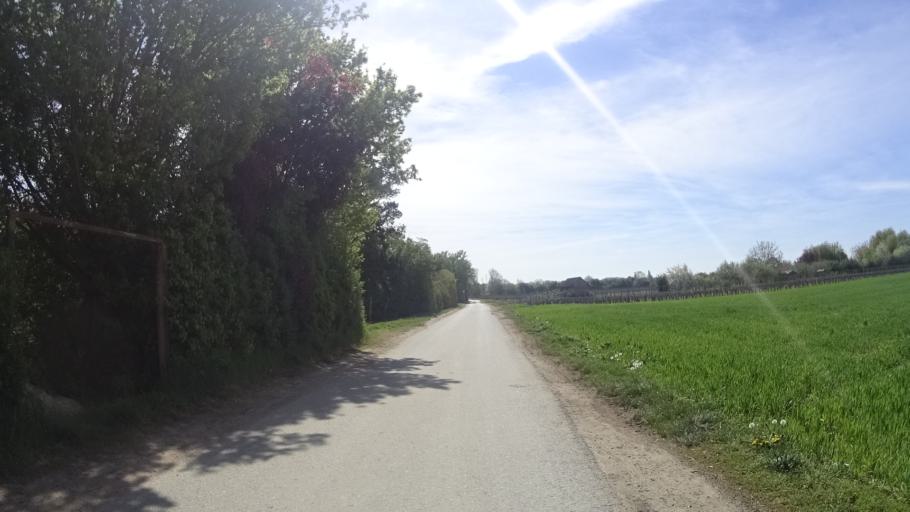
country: DE
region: Rheinland-Pfalz
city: Oppenheim
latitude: 49.8443
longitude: 8.3653
